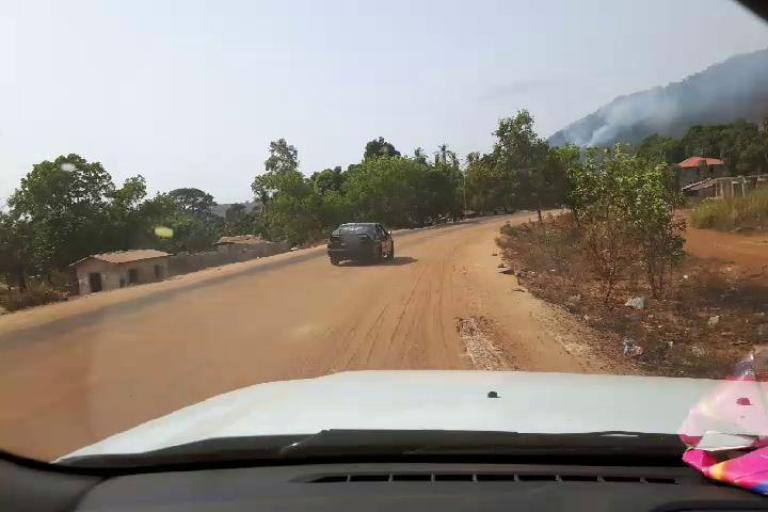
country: SL
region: Western Area
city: Waterloo
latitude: 8.2434
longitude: -13.1529
